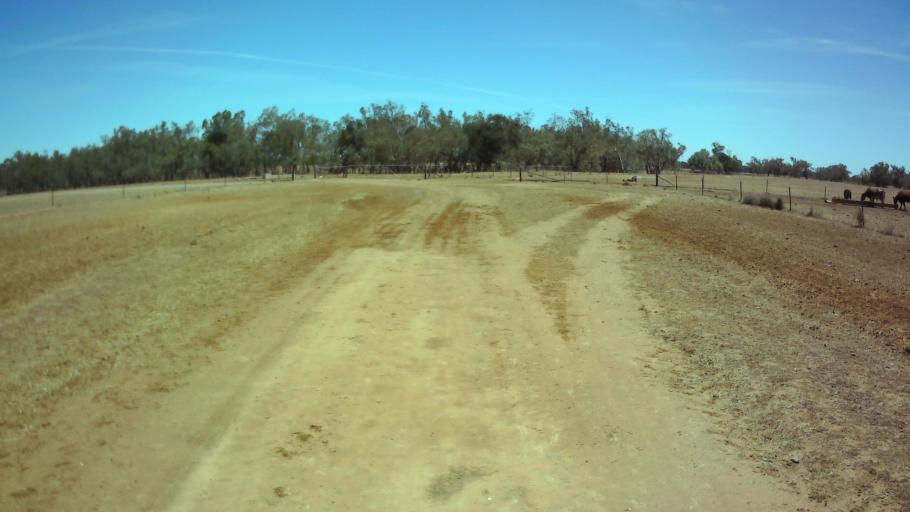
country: AU
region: New South Wales
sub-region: Bland
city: West Wyalong
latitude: -33.8312
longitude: 147.6365
